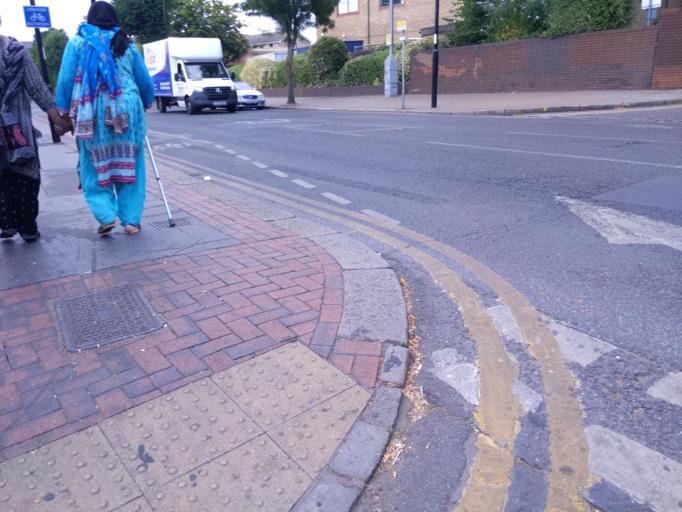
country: GB
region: England
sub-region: Greater London
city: Croydon
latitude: 51.3898
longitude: -0.1121
